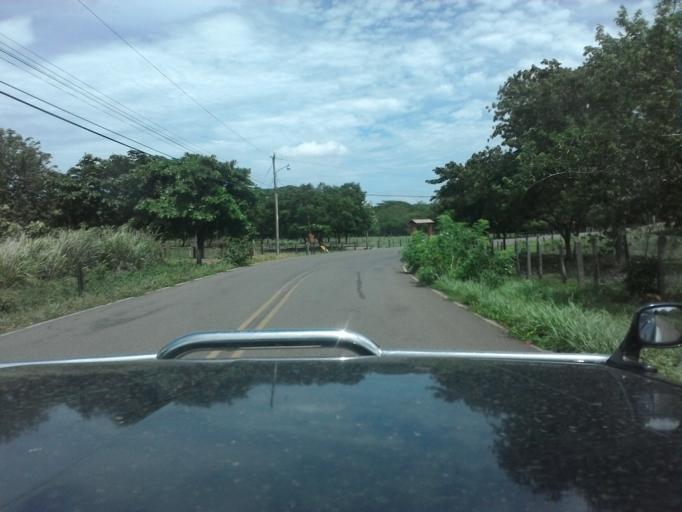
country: CR
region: Puntarenas
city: Miramar
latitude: 10.1327
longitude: -84.8341
